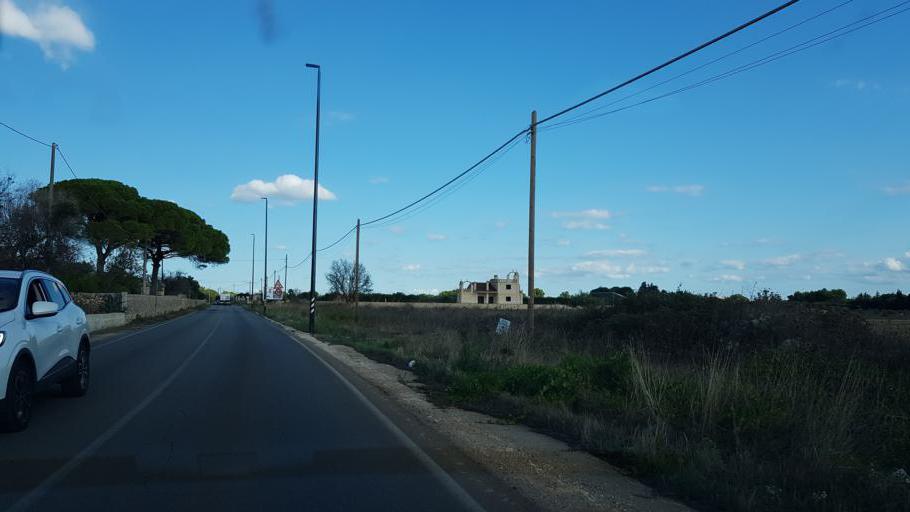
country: IT
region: Apulia
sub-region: Provincia di Lecce
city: Nardo
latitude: 40.1279
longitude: 18.0230
